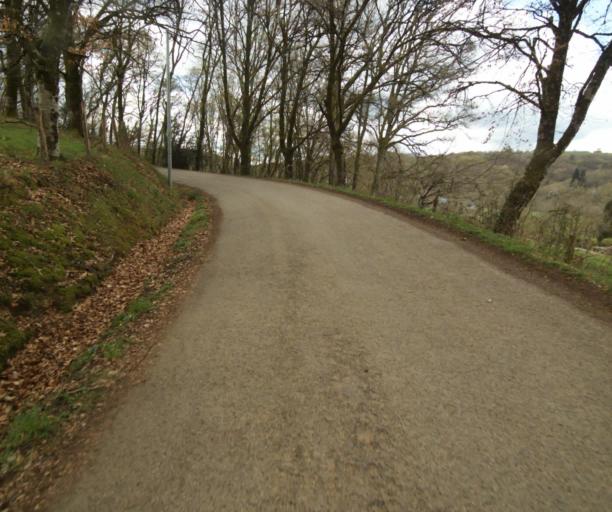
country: FR
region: Limousin
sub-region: Departement de la Correze
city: Laguenne
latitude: 45.2491
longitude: 1.8484
